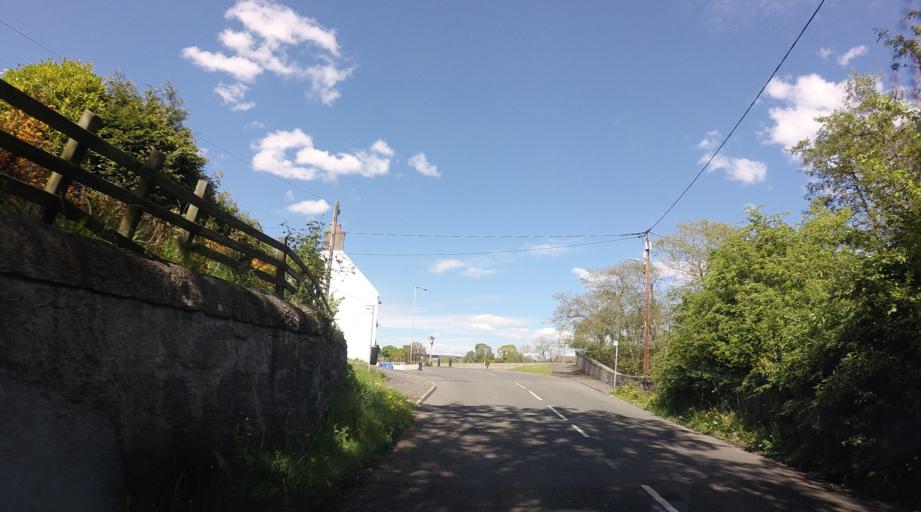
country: GB
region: Scotland
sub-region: West Lothian
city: Linlithgow
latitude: 55.9765
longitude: -3.6313
